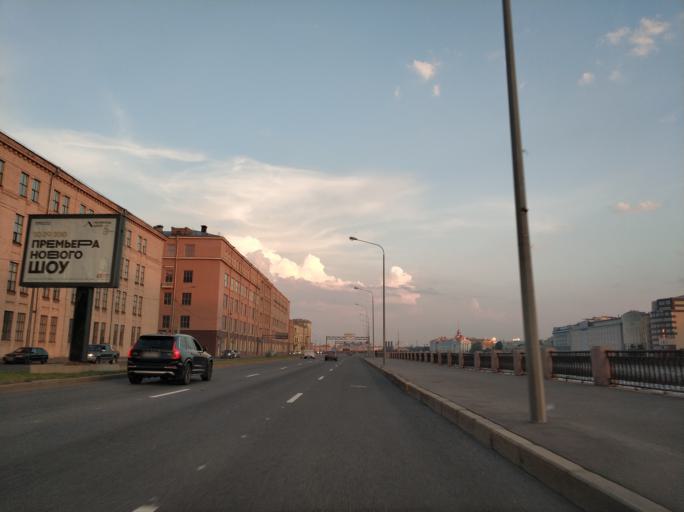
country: RU
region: Leningrad
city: Sampsonievskiy
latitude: 59.9637
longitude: 30.3376
